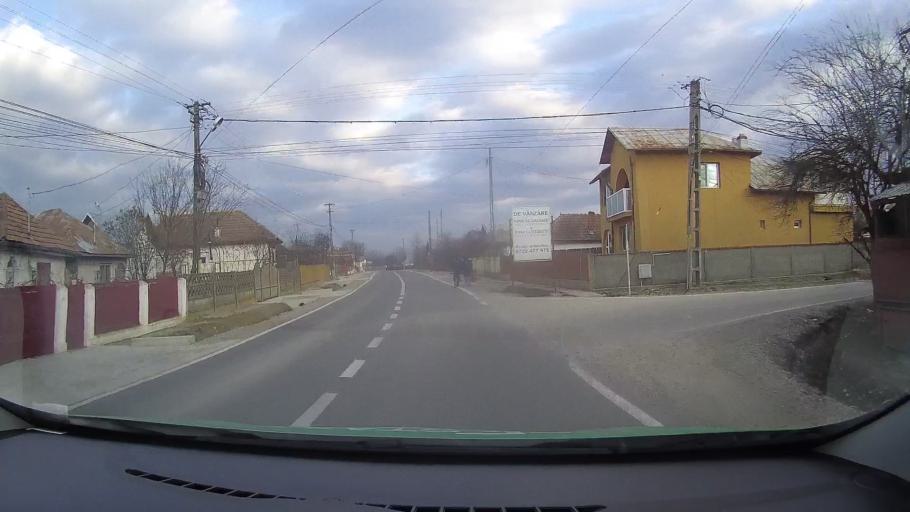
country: RO
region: Dambovita
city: Ion Luca Caragiale
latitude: 44.9138
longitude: 25.6938
